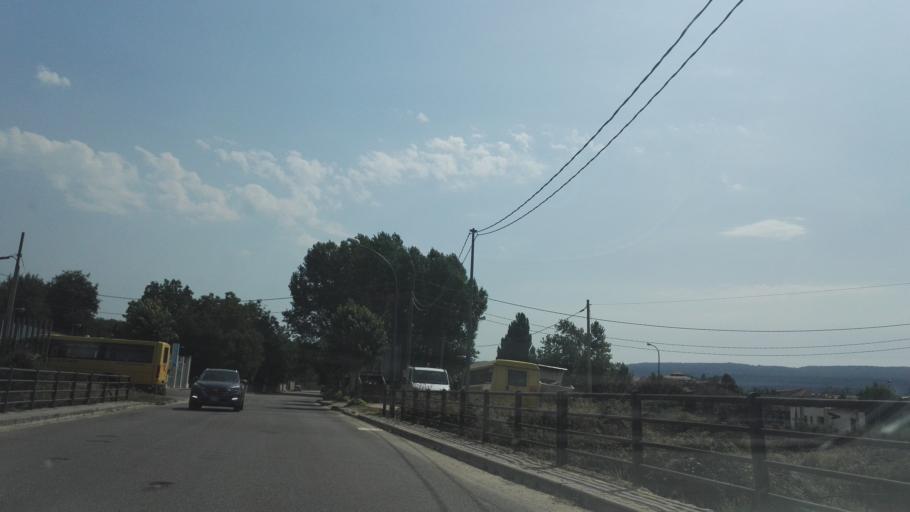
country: IT
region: Calabria
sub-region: Provincia di Vibo-Valentia
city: Serra San Bruno
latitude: 38.5768
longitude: 16.3324
